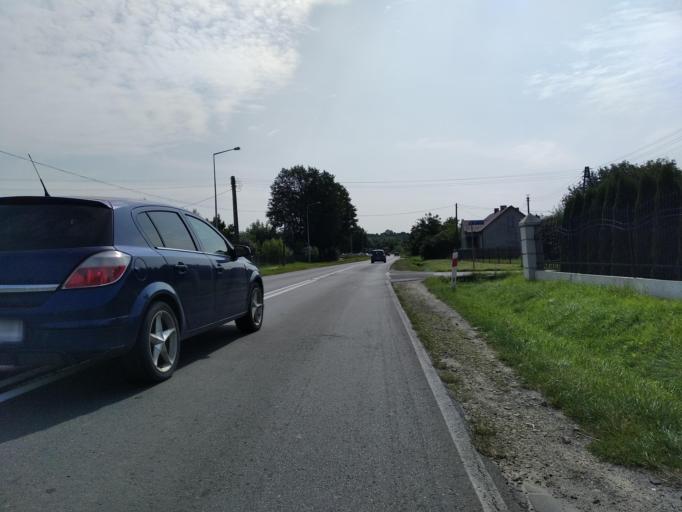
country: PL
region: Subcarpathian Voivodeship
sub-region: Powiat ropczycko-sedziszowski
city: Ostrow
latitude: 50.0720
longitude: 21.5866
